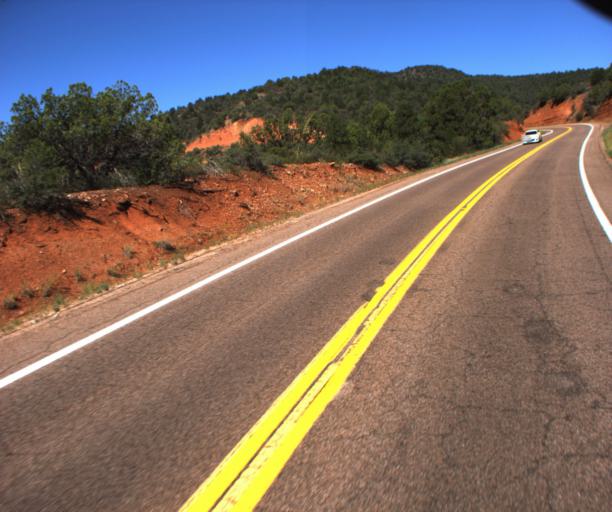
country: US
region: Arizona
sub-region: Navajo County
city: Cibecue
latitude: 33.9318
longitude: -110.3447
